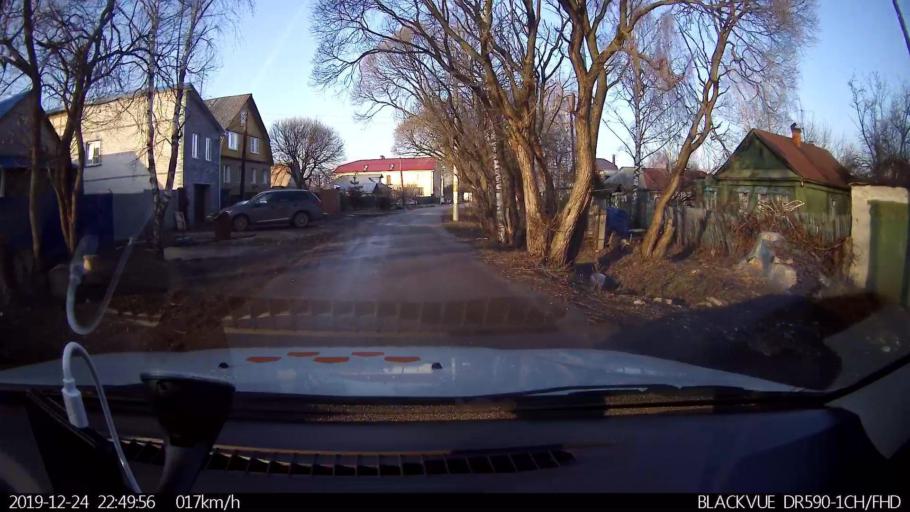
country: RU
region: Nizjnij Novgorod
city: Nizhniy Novgorod
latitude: 56.2883
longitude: 43.8995
